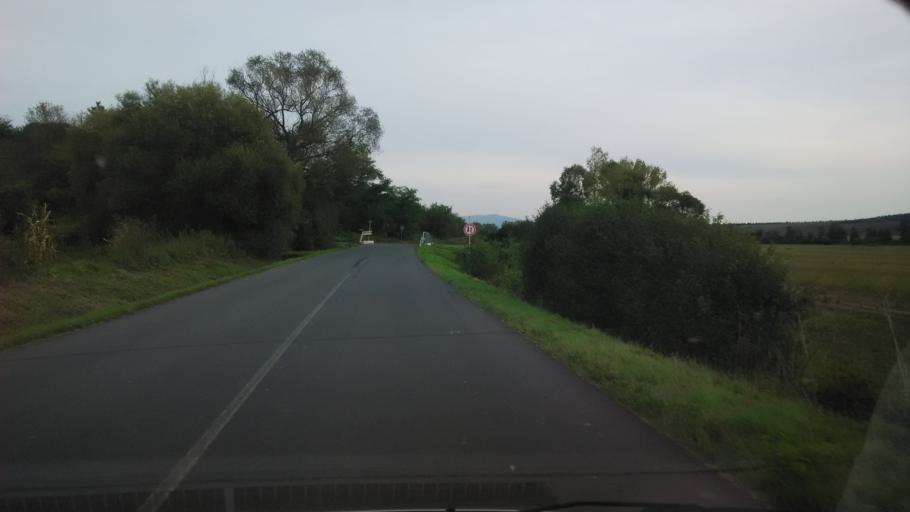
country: SK
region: Banskobystricky
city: Dudince
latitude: 48.1734
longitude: 18.8571
